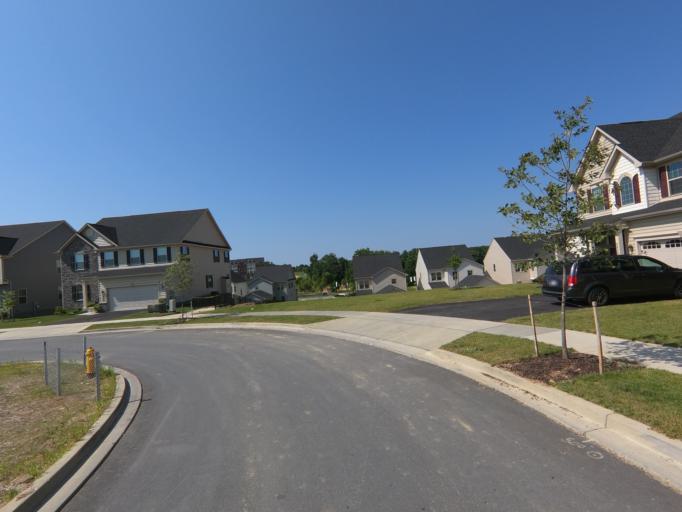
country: US
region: Maryland
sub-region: Frederick County
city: Spring Ridge
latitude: 39.3959
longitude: -77.3159
